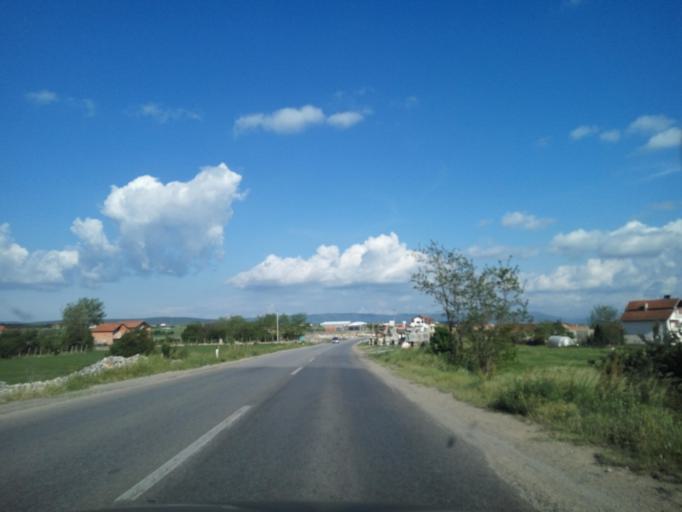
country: XK
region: Prizren
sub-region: Komuna e Malisheves
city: Llazice
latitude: 42.5774
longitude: 20.7035
